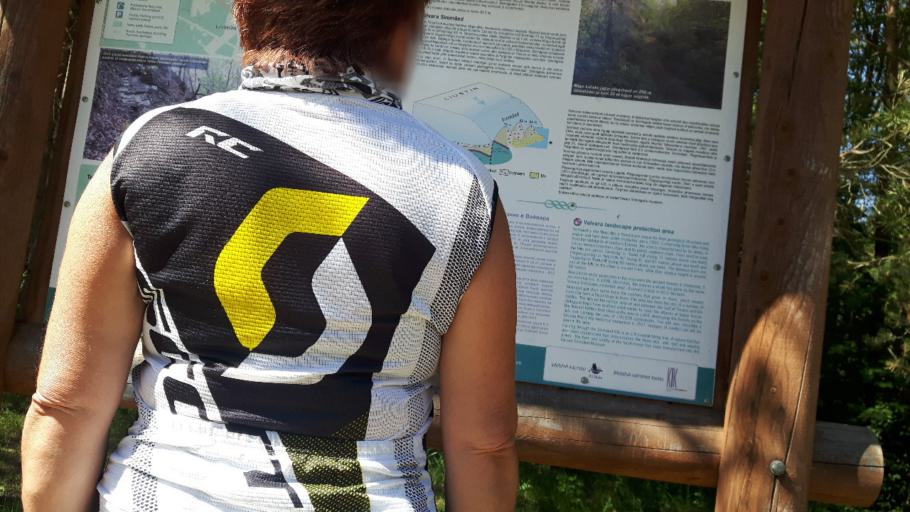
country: EE
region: Ida-Virumaa
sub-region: Sillamaee linn
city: Sillamae
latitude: 59.3743
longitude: 27.8553
